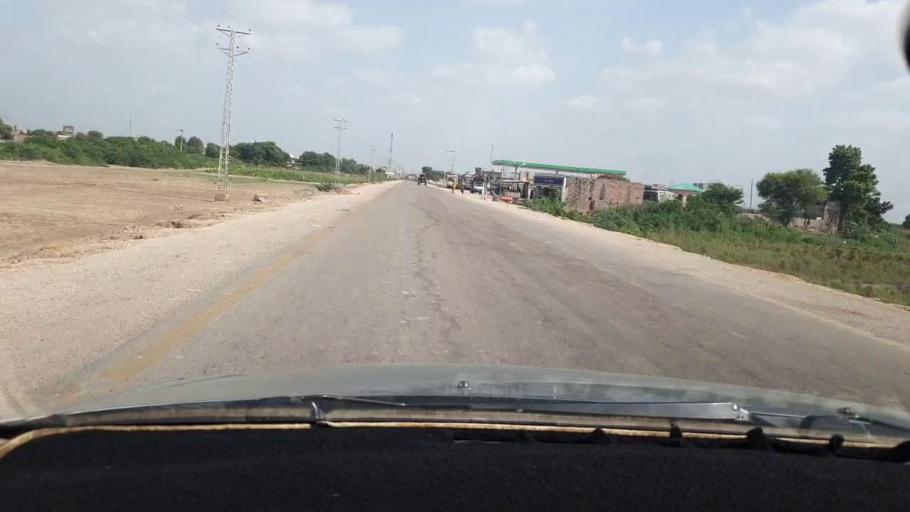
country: PK
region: Sindh
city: Naukot
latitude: 24.8608
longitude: 69.3923
